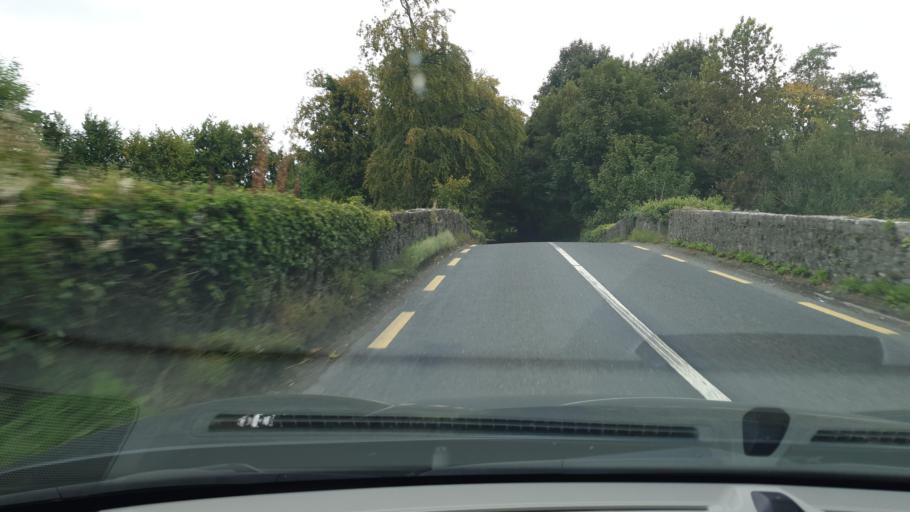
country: IE
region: Leinster
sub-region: Kildare
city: Sallins
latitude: 53.2641
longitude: -6.6801
